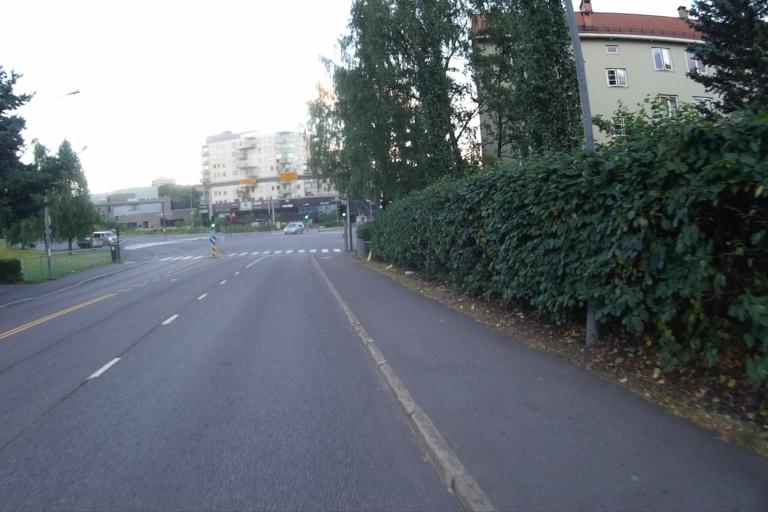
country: NO
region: Oslo
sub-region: Oslo
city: Oslo
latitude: 59.9246
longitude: 10.7902
